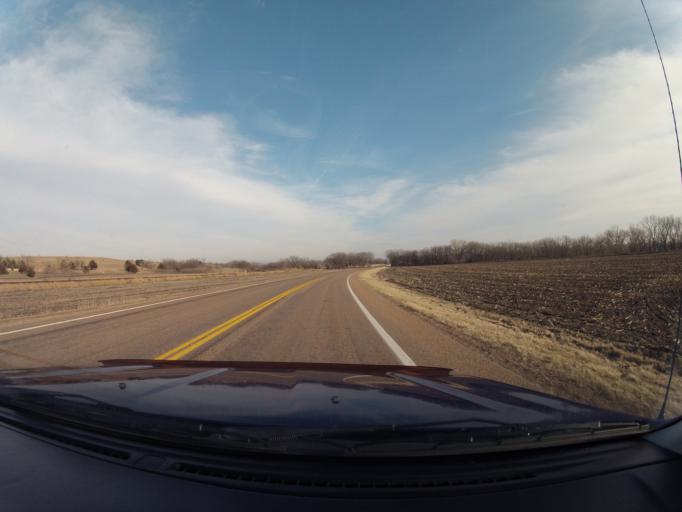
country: US
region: Kansas
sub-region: Pottawatomie County
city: Saint Marys
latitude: 39.2165
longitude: -96.1223
